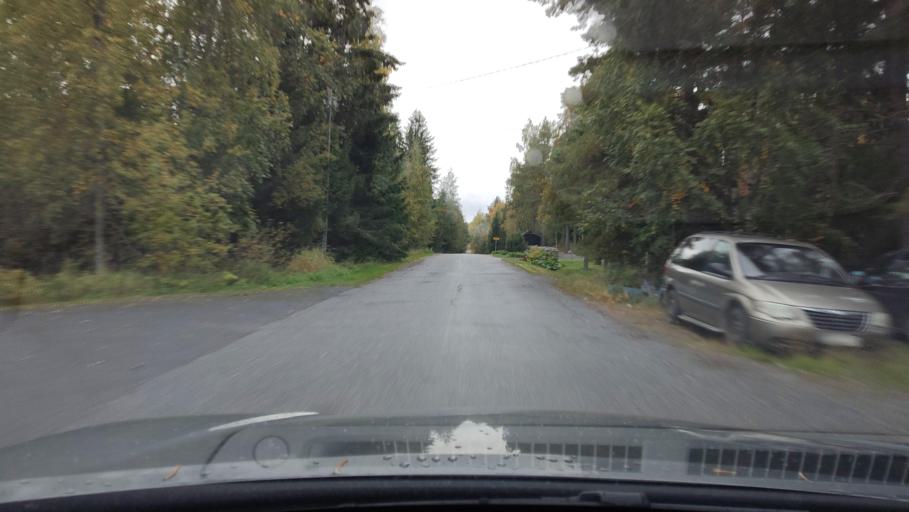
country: FI
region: Ostrobothnia
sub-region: Sydosterbotten
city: Kristinestad
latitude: 62.2650
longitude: 21.4630
